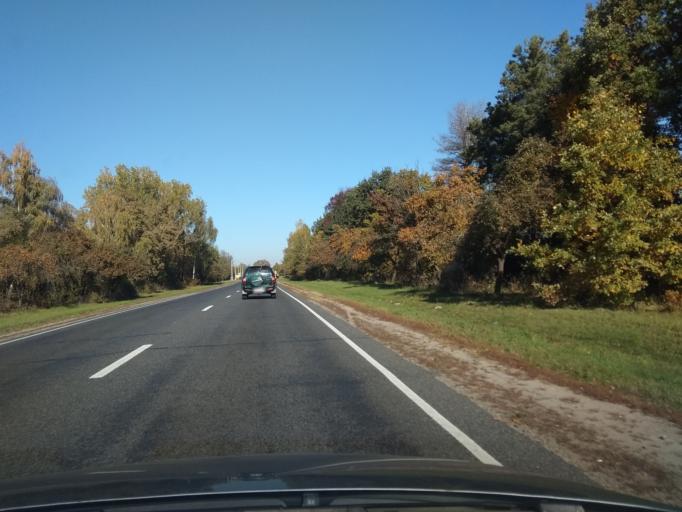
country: BY
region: Brest
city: Kobryn
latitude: 52.1546
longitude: 24.3090
